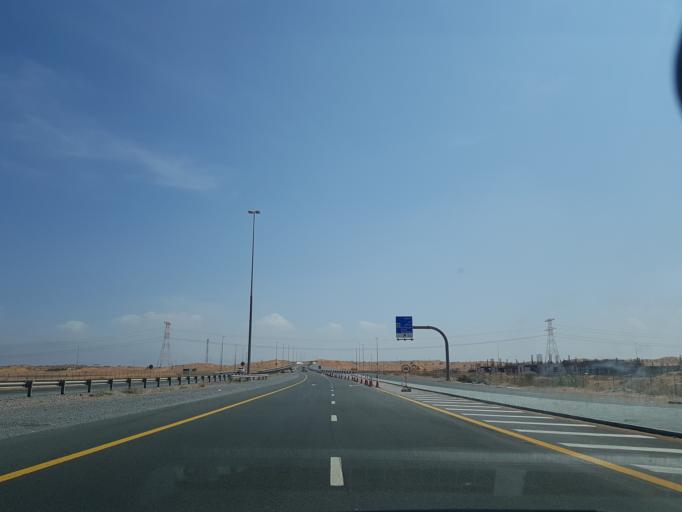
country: AE
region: Ra's al Khaymah
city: Ras al-Khaimah
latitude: 25.6677
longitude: 55.8910
